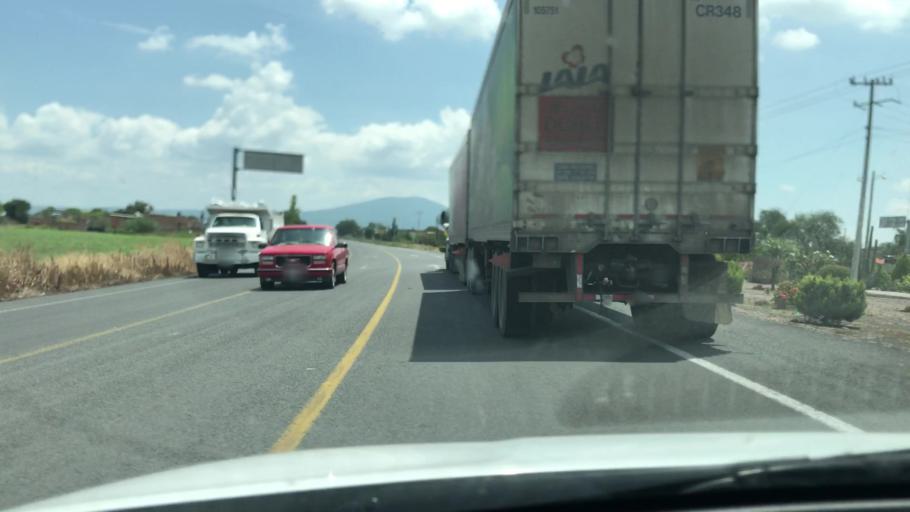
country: MX
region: Michoacan
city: Tanhuato de Guerrero
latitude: 20.2858
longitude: -102.3398
